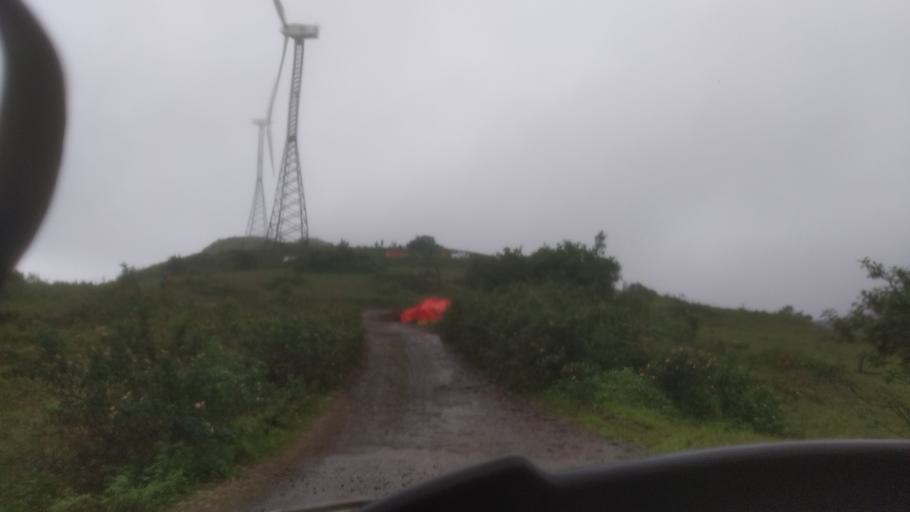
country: IN
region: Tamil Nadu
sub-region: Theni
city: Kombai
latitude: 9.8880
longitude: 77.2212
